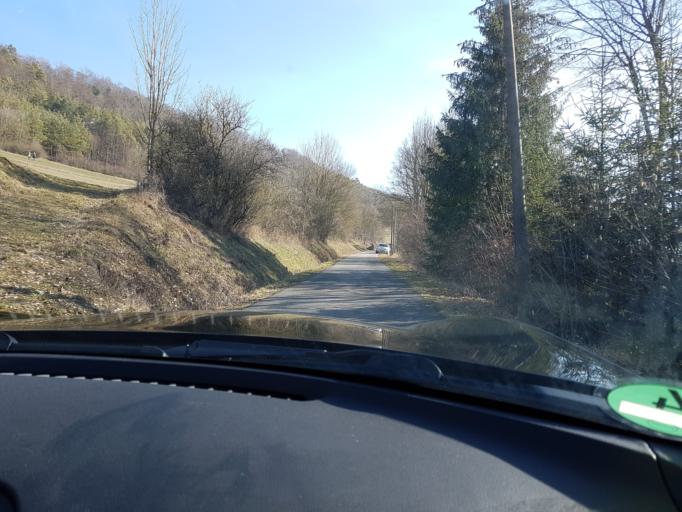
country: DE
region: Baden-Wuerttemberg
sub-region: Regierungsbezirk Stuttgart
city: Langenburg
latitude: 49.2974
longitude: 9.8318
